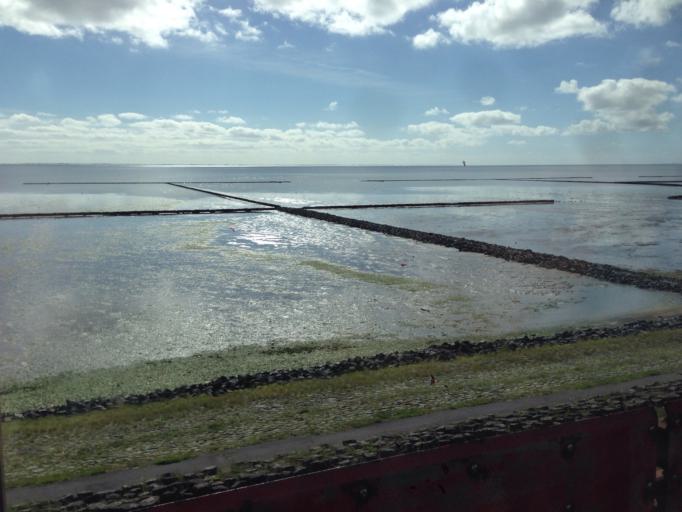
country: DE
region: Schleswig-Holstein
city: Friedrich-Wilhelm-Lubke-Koog
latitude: 54.8837
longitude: 8.5298
